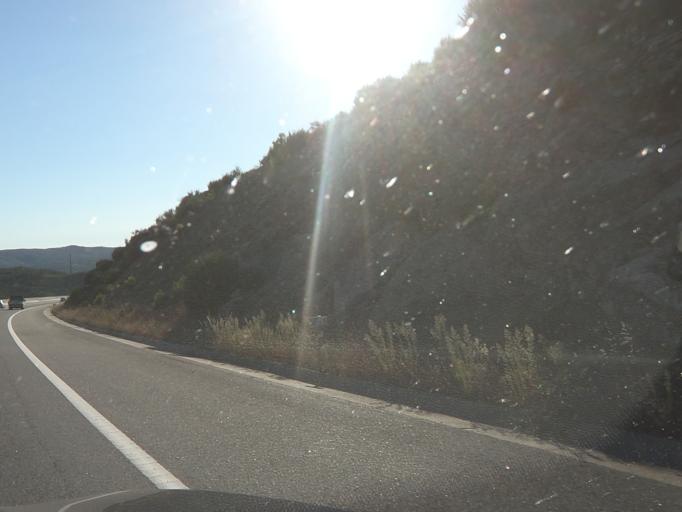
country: PT
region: Vila Real
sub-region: Sabrosa
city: Sabrosa
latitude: 41.3639
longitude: -7.5591
